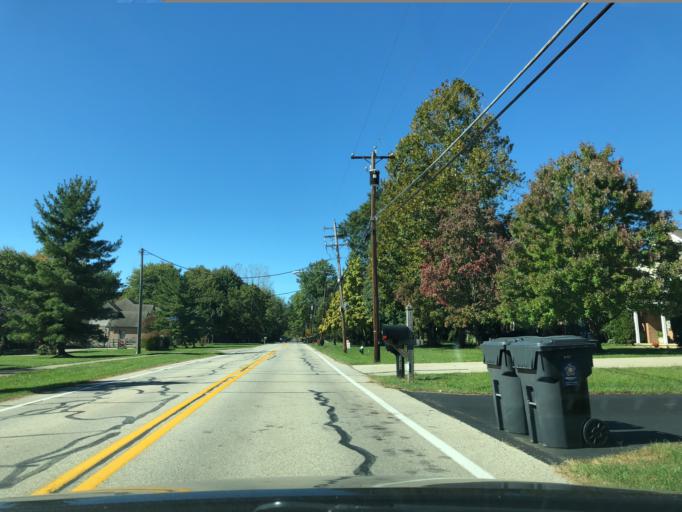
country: US
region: Ohio
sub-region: Hamilton County
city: Sixteen Mile Stand
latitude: 39.2747
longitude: -84.3083
